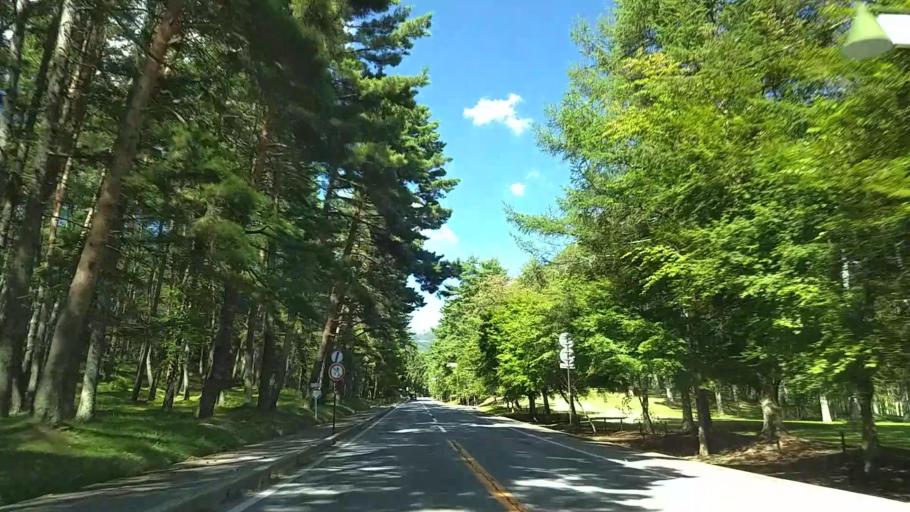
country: JP
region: Nagano
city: Chino
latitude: 36.0459
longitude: 138.2485
